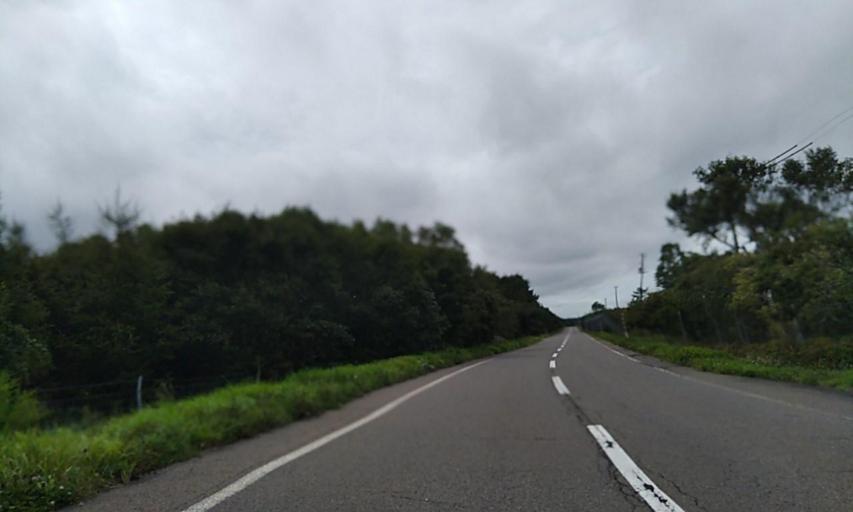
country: JP
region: Hokkaido
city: Nemuro
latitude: 43.3663
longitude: 145.2794
